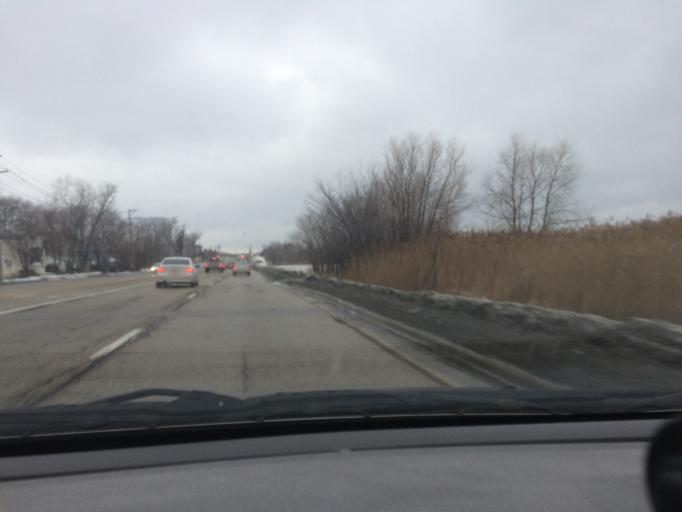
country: US
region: Illinois
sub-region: DuPage County
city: Hanover Park
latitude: 41.9728
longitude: -88.1211
